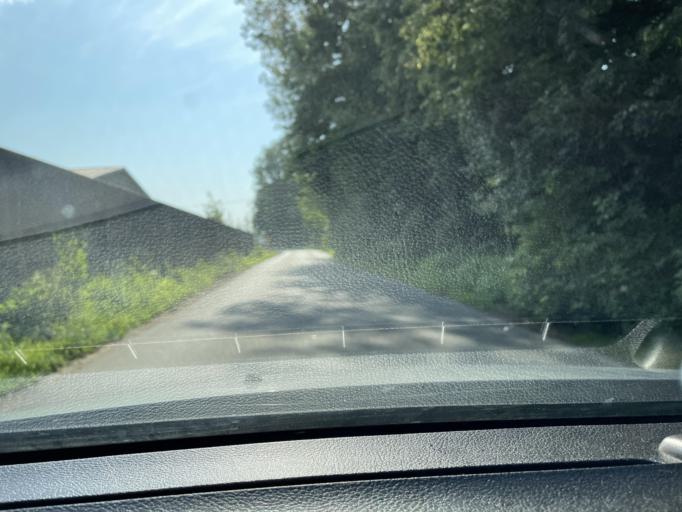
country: DE
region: Bavaria
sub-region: Upper Bavaria
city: Muehldorf
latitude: 48.2418
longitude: 12.5457
